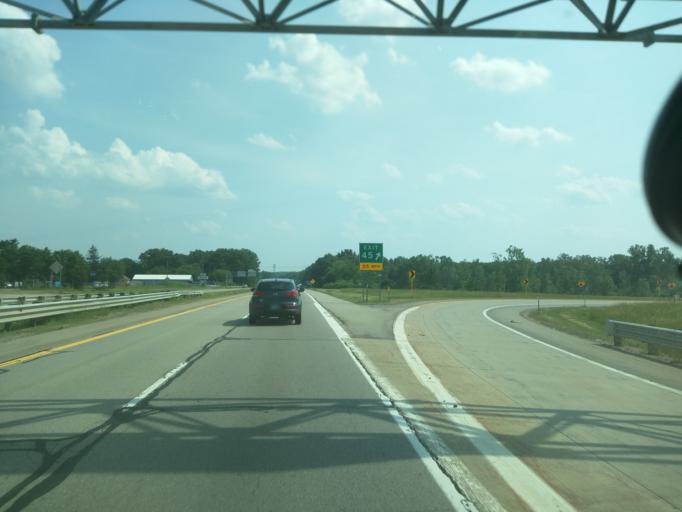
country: US
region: Michigan
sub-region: Jackson County
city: Jackson
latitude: 42.2907
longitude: -84.4329
